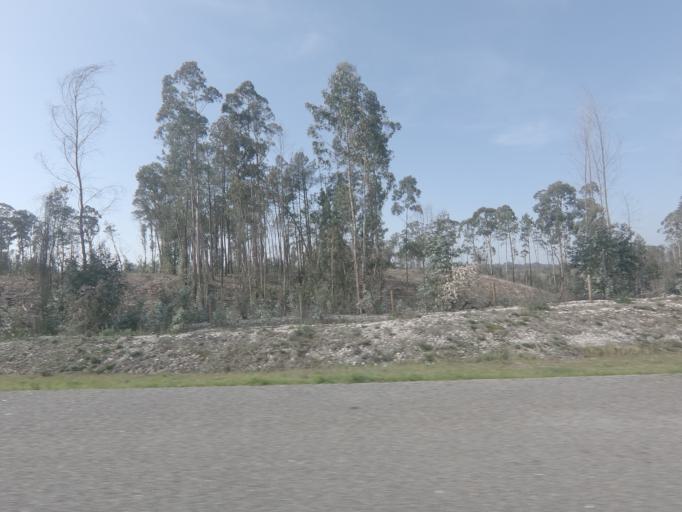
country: PT
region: Aveiro
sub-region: Aveiro
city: Eixo
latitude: 40.6052
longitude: -8.5510
